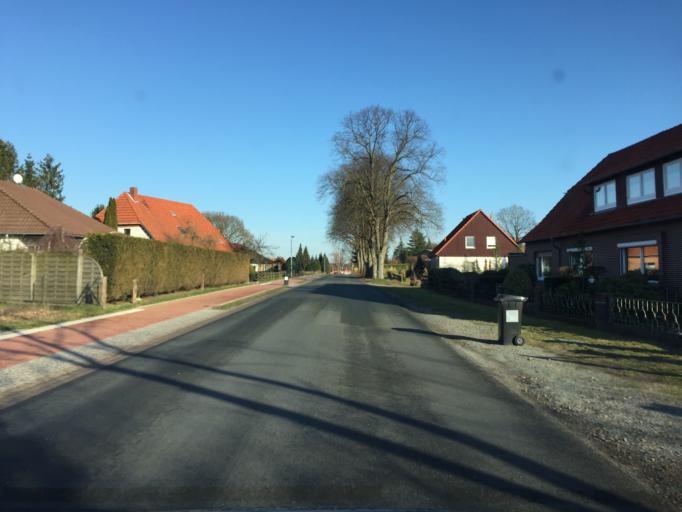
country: DE
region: Lower Saxony
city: Husum
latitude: 52.5617
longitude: 9.2467
